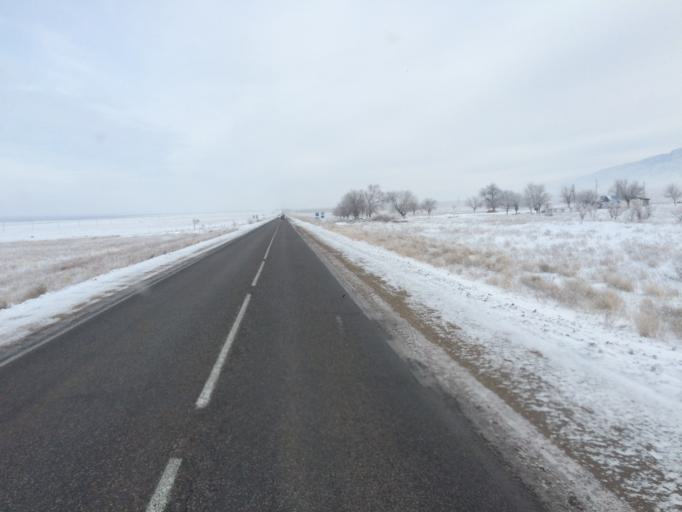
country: KG
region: Chuy
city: Ivanovka
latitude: 43.3794
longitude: 75.2181
